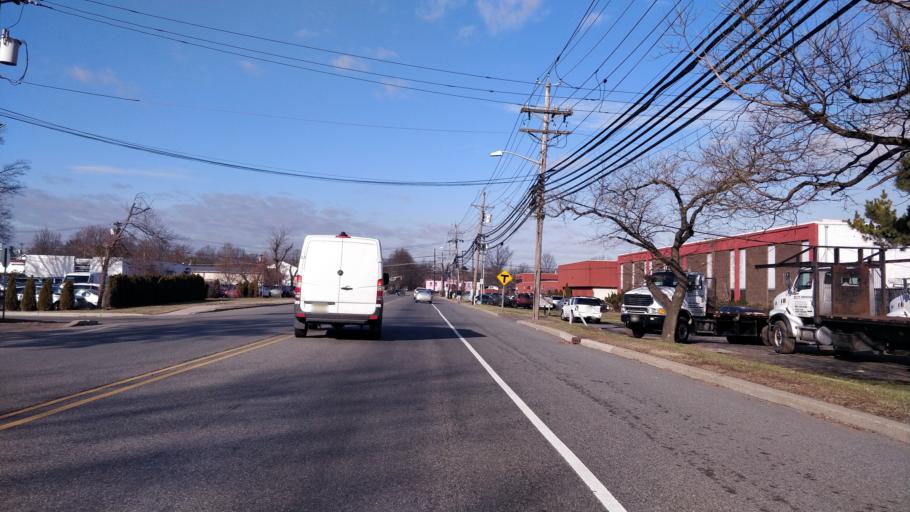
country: US
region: New Jersey
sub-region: Middlesex County
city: South Plainfield
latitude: 40.5779
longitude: -74.4311
